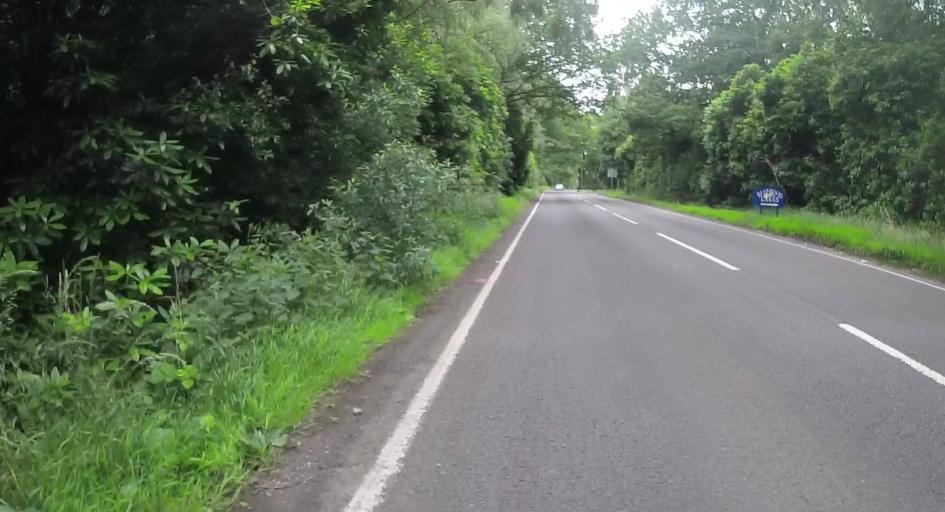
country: GB
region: England
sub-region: Wokingham
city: Winnersh
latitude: 51.4138
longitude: -0.8774
